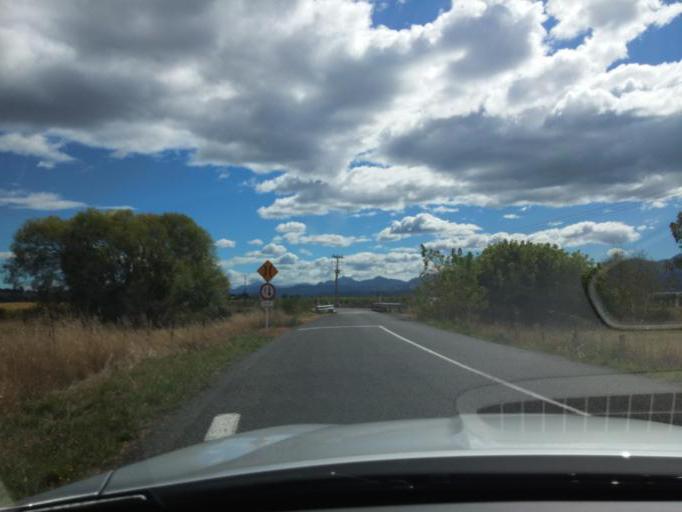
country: NZ
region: Marlborough
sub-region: Marlborough District
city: Blenheim
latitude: -41.5266
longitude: 173.8369
